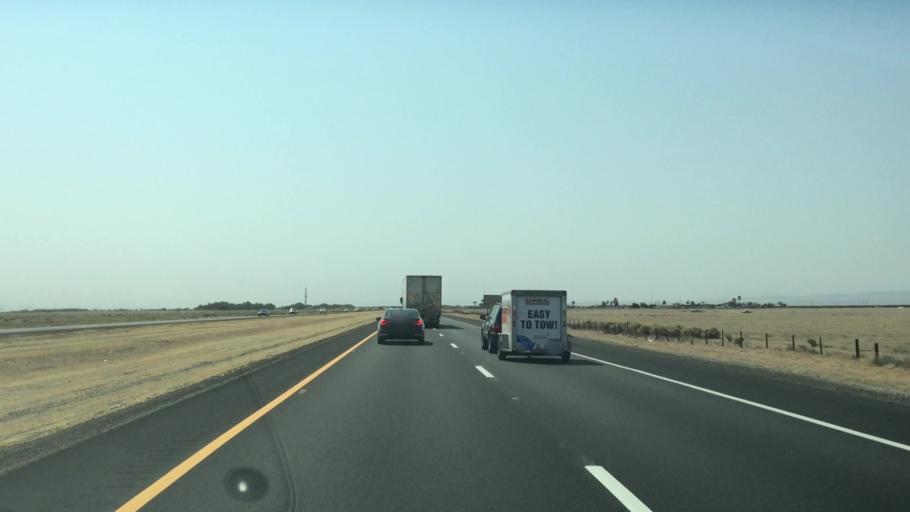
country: US
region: California
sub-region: Kern County
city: Lost Hills
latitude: 35.6310
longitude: -119.6644
